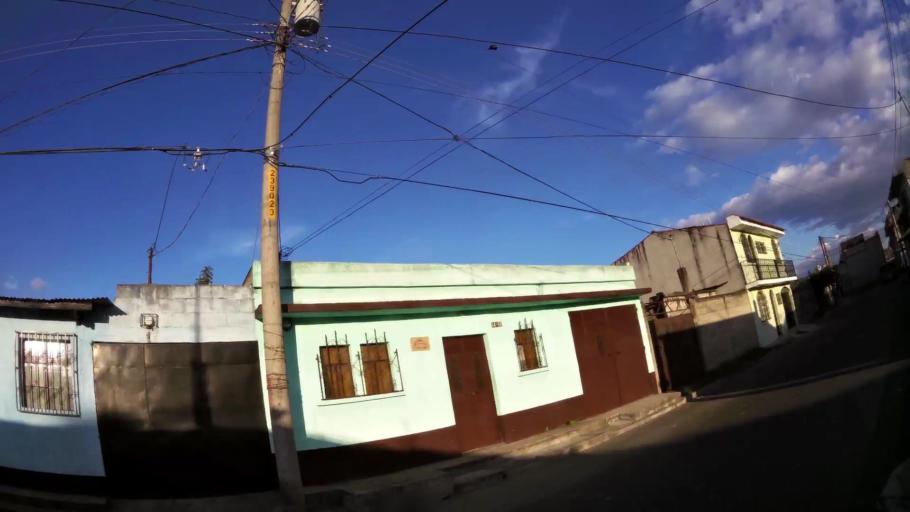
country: GT
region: Guatemala
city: Villa Nueva
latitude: 14.5146
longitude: -90.5830
